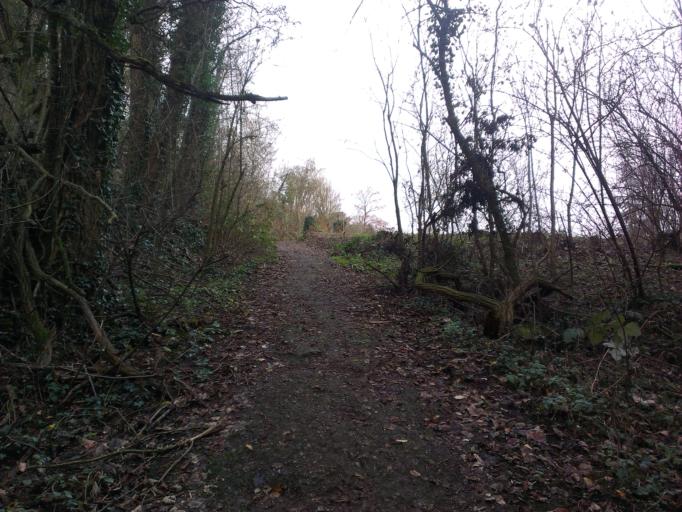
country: DE
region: Baden-Wuerttemberg
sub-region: Karlsruhe Region
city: Hemsbach
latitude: 49.5783
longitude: 8.6683
